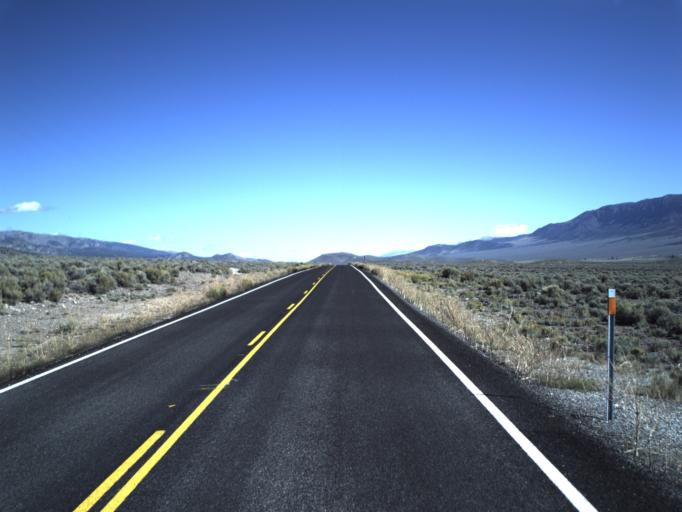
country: US
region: Utah
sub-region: Piute County
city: Junction
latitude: 38.1922
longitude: -112.0116
